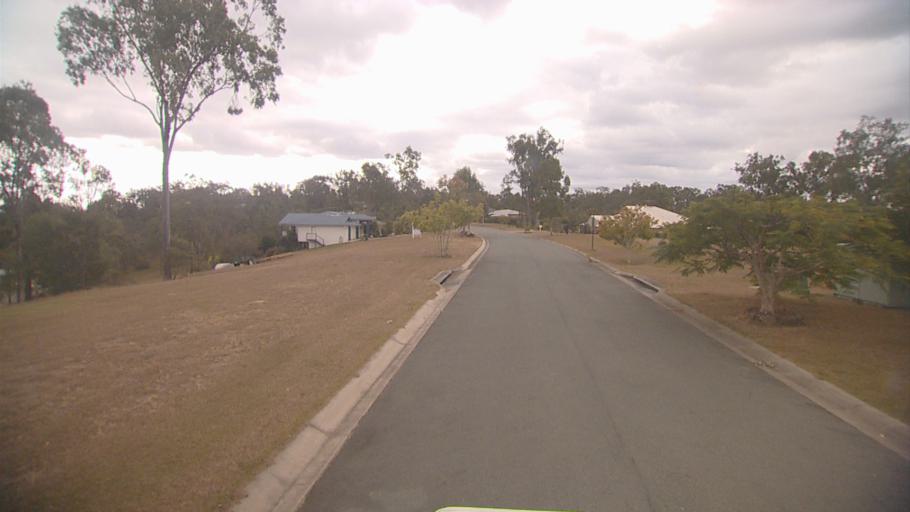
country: AU
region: Queensland
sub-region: Logan
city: Cedar Vale
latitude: -27.8737
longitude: 153.0744
